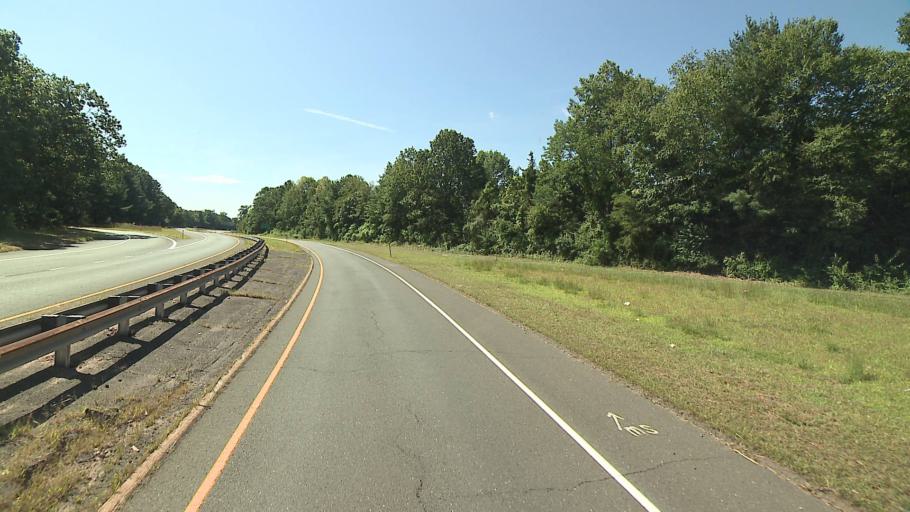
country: US
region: Connecticut
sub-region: Hartford County
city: Tariffville
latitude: 41.8939
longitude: -72.7508
